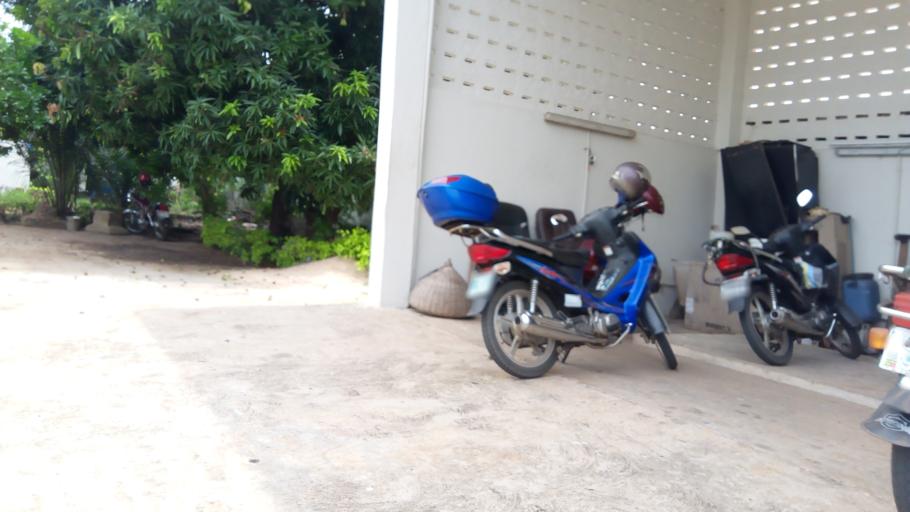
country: TG
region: Maritime
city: Lome
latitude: 6.1280
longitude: 1.2125
